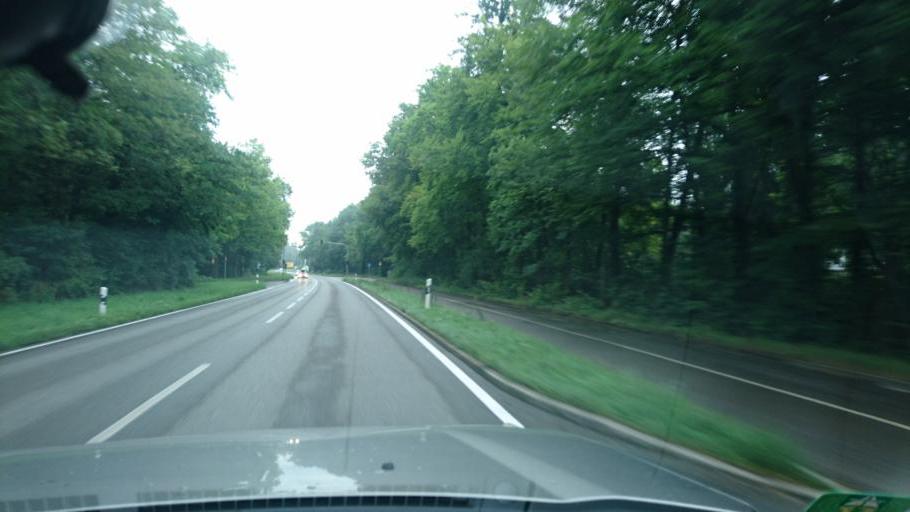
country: DE
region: Baden-Wuerttemberg
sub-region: Freiburg Region
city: Singen
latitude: 47.7497
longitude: 8.8163
